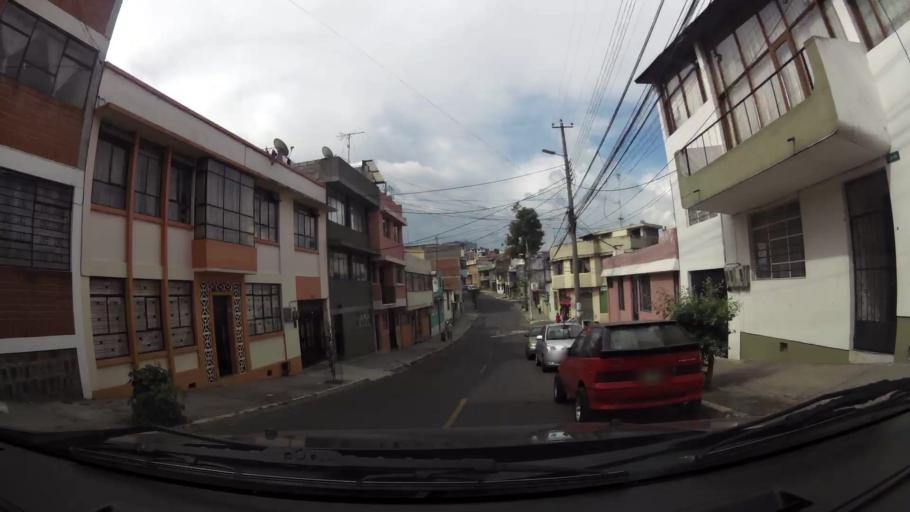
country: EC
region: Pichincha
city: Quito
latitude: -0.2146
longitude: -78.4855
